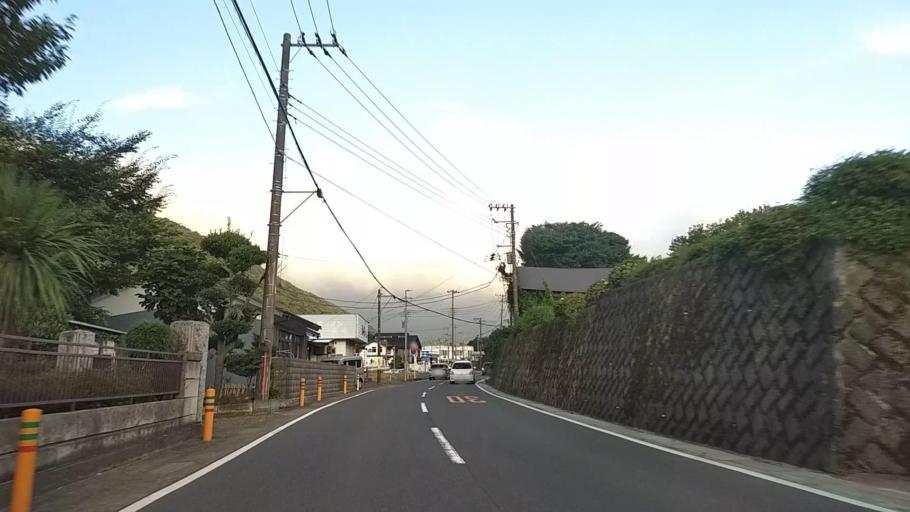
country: JP
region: Kanagawa
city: Atsugi
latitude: 35.4837
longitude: 139.2752
